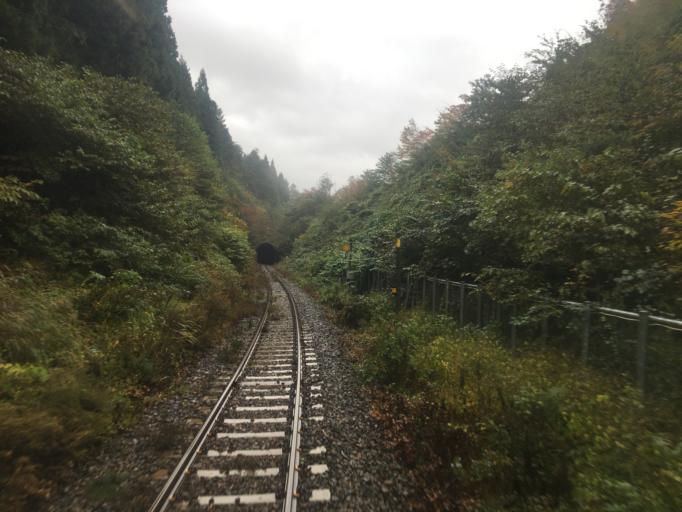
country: JP
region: Yamagata
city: Shinjo
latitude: 38.7651
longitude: 140.4647
